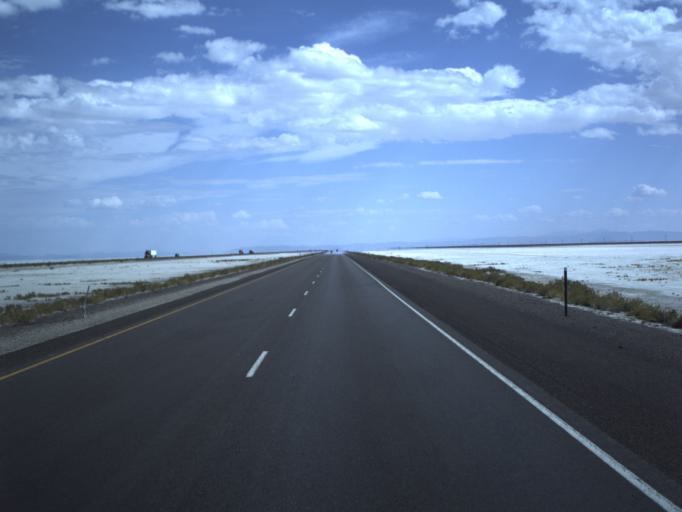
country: US
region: Utah
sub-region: Tooele County
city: Wendover
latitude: 40.7360
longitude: -113.7319
